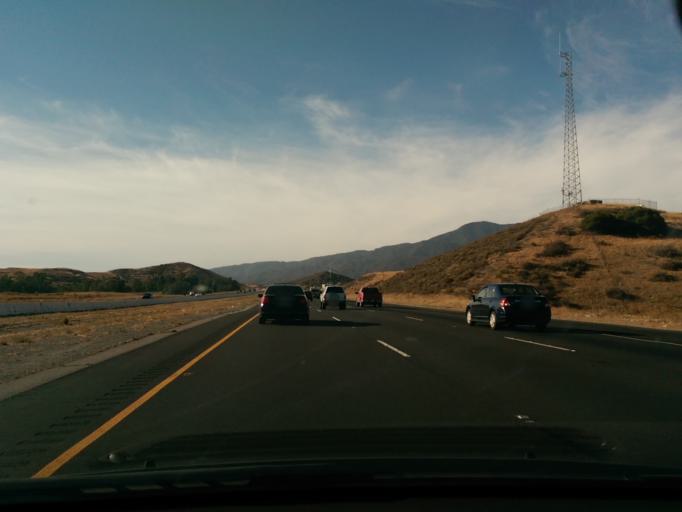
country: US
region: California
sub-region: Riverside County
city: El Cerrito
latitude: 33.7823
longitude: -117.4908
